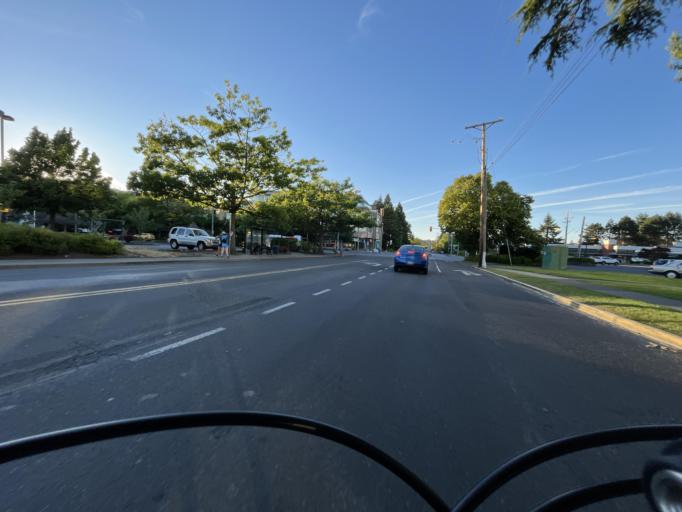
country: CA
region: British Columbia
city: Oak Bay
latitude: 48.4316
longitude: -123.3224
